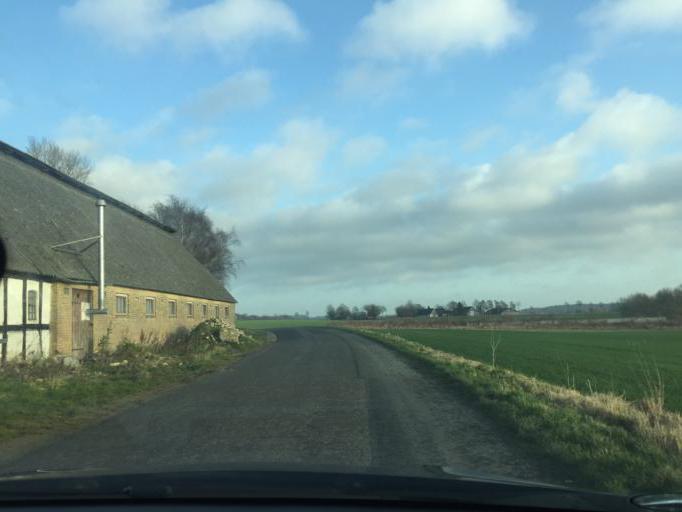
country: DK
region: South Denmark
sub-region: Odense Kommune
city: Bellinge
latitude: 55.2000
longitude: 10.3332
